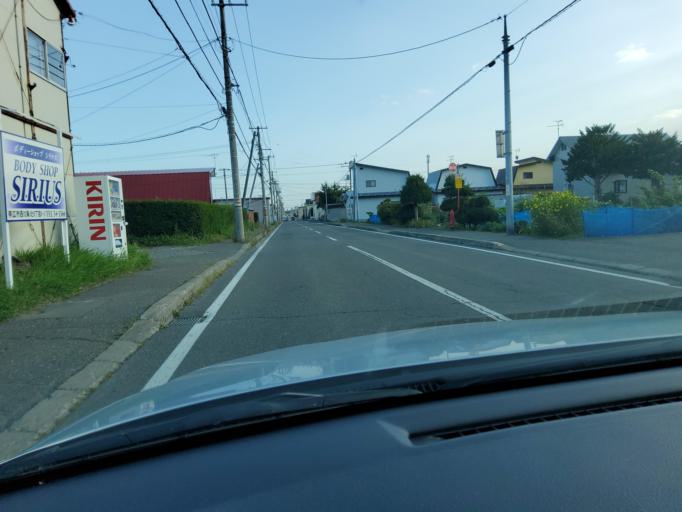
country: JP
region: Hokkaido
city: Obihiro
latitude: 42.9378
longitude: 143.1828
